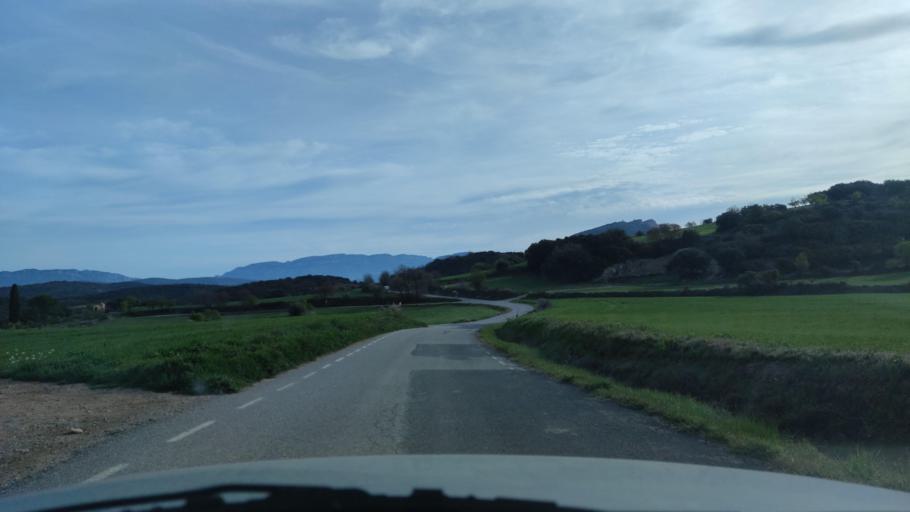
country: ES
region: Catalonia
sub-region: Provincia de Lleida
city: Os de Balaguer
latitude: 41.8798
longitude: 0.7879
